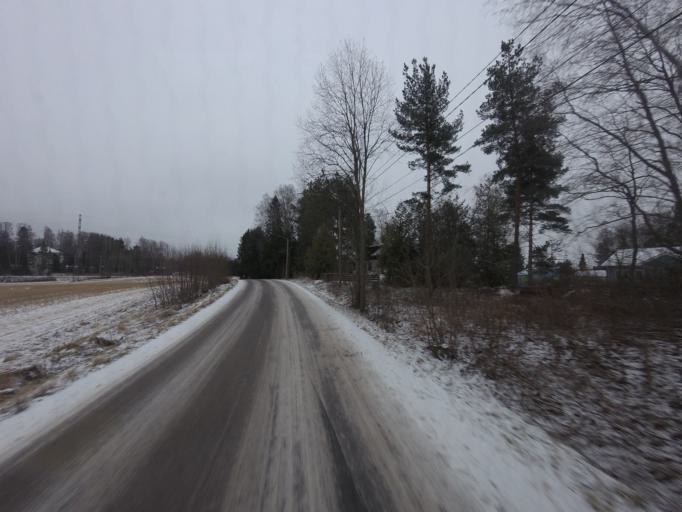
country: FI
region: Uusimaa
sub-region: Helsinki
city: Espoo
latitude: 60.1971
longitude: 24.5654
